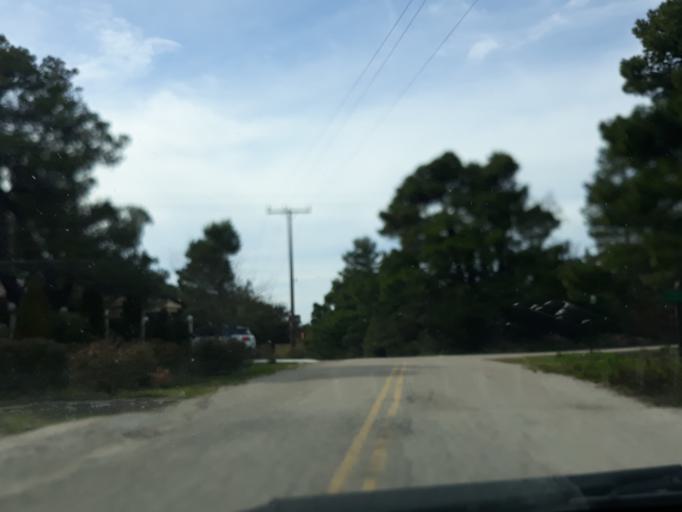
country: GR
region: Attica
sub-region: Nomarchia Anatolikis Attikis
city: Afidnes
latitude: 38.2149
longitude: 23.7924
